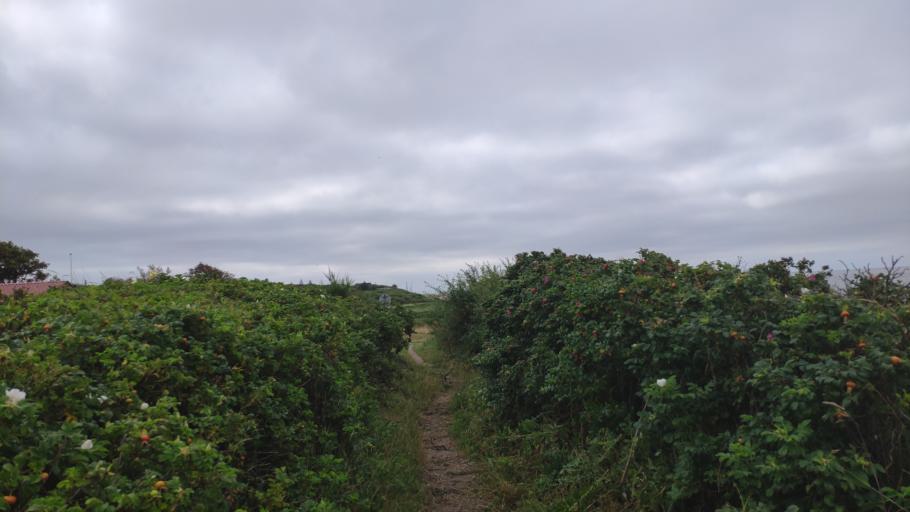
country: DK
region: South Denmark
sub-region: Varde Kommune
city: Oksbol
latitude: 55.5347
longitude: 8.3395
